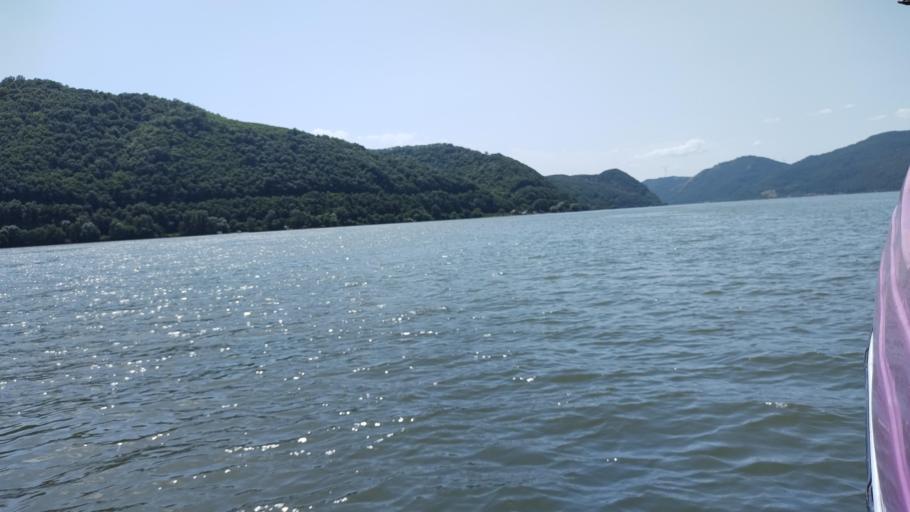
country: RS
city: Radenka
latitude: 44.6563
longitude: 21.8075
